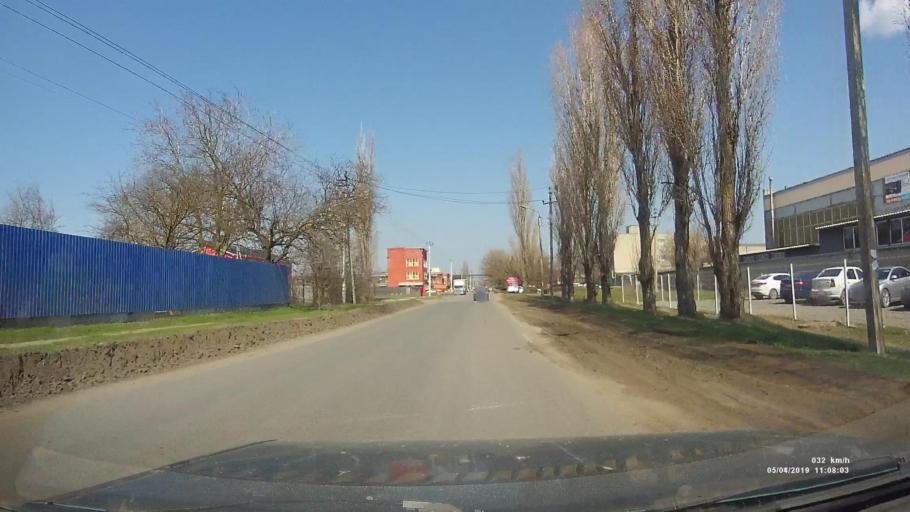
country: RU
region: Rostov
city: Azov
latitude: 47.0841
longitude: 39.4365
